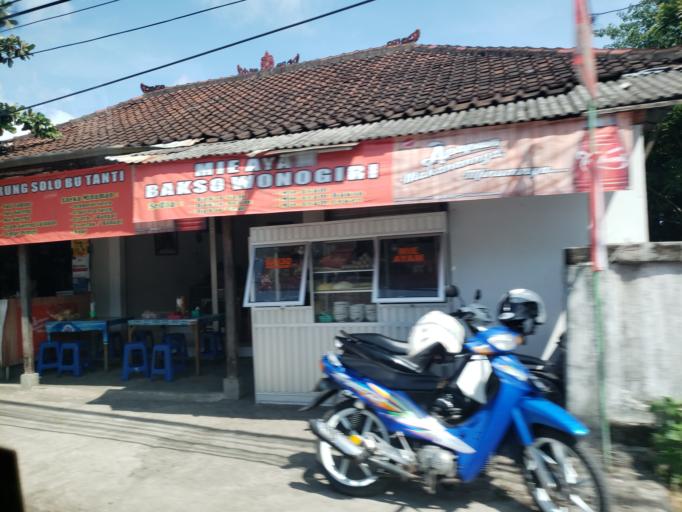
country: ID
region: Bali
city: Kangin
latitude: -8.8273
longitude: 115.1395
